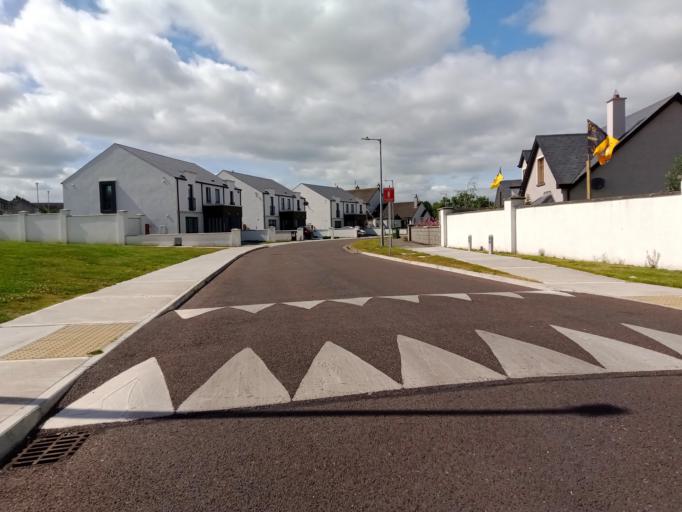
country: IE
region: Leinster
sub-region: Kilkenny
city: Callan
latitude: 52.5409
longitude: -7.3854
